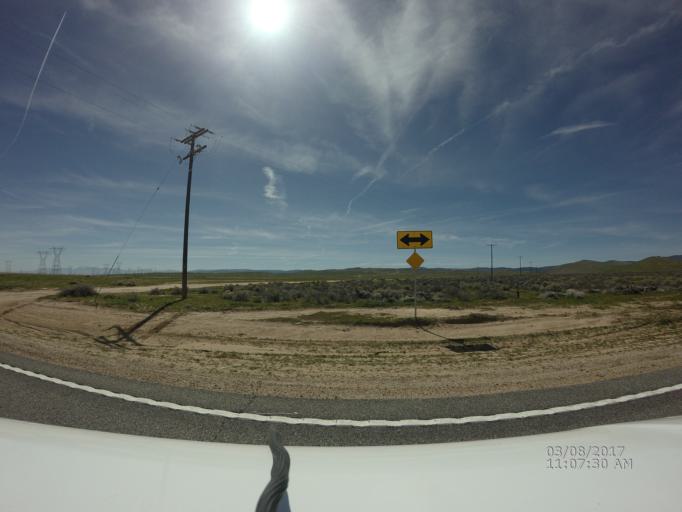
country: US
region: California
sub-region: Los Angeles County
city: Green Valley
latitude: 34.7755
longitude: -118.3787
